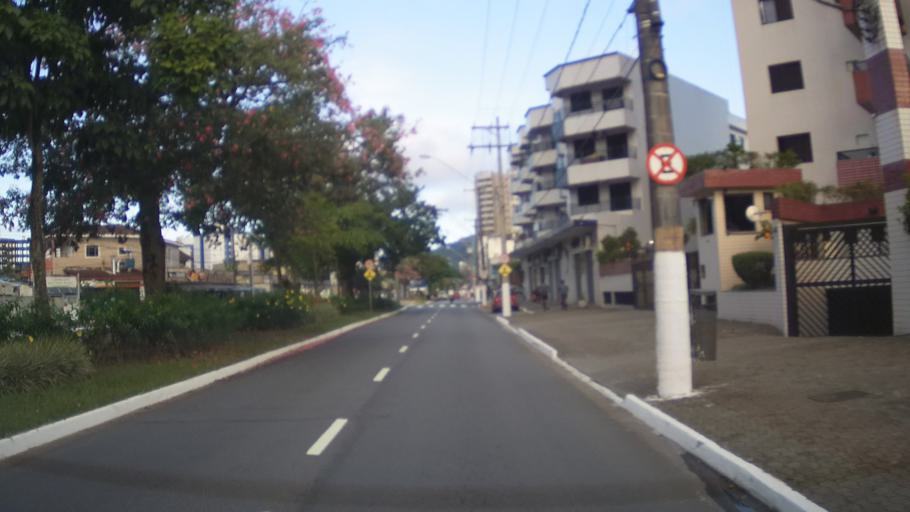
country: BR
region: Sao Paulo
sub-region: Praia Grande
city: Praia Grande
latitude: -24.0029
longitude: -46.4103
